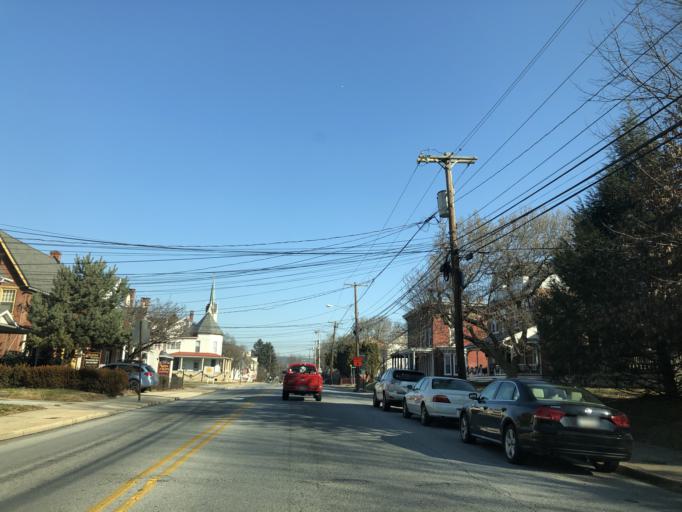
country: US
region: Pennsylvania
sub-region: Chester County
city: Downingtown
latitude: 40.0088
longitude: -75.6982
